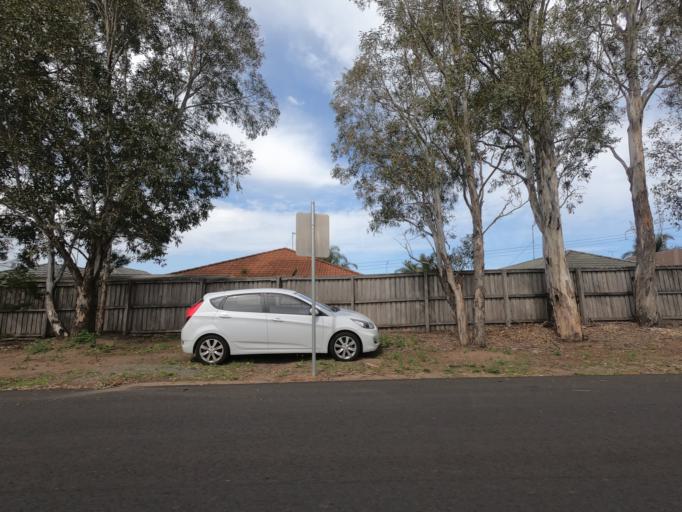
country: AU
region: New South Wales
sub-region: Wollongong
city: Dapto
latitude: -34.4884
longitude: 150.7670
